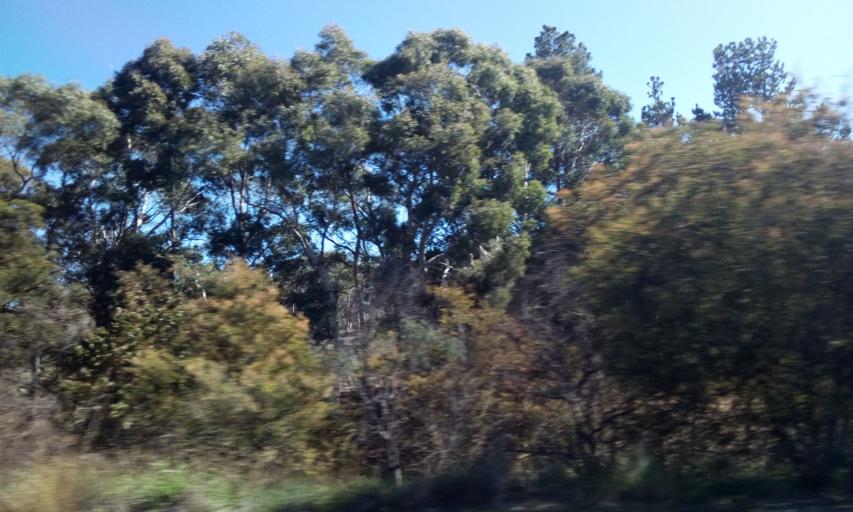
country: AU
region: New South Wales
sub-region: Yass Valley
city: Gundaroo
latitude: -35.1505
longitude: 149.3304
